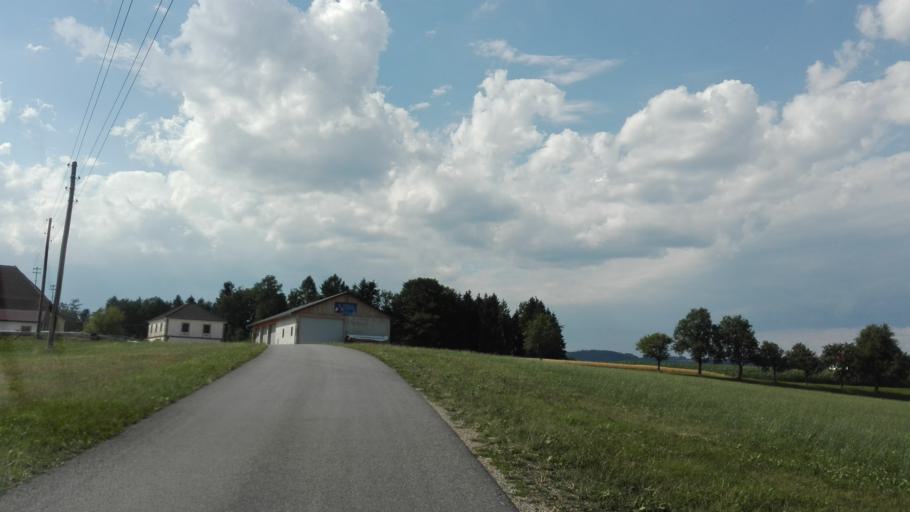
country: AT
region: Upper Austria
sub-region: Politischer Bezirk Perg
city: Perg
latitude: 48.2433
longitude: 14.7051
